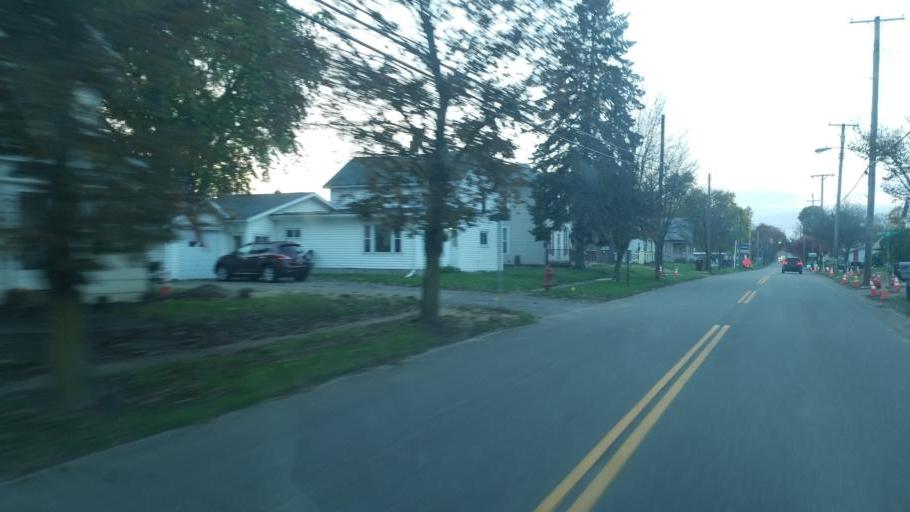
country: US
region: Ohio
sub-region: Ashland County
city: Loudonville
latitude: 40.6563
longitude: -82.3100
